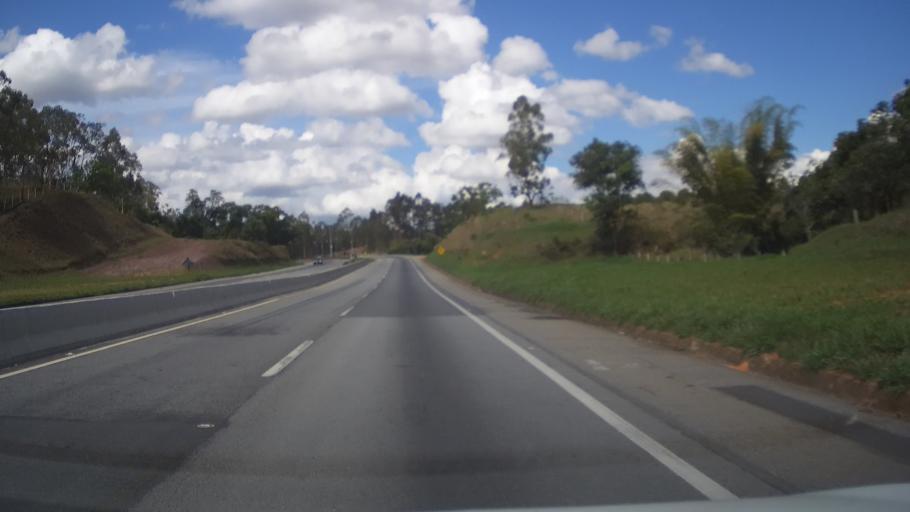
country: BR
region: Minas Gerais
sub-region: Santo Antonio Do Amparo
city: Santo Antonio do Amparo
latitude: -20.8610
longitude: -44.8394
